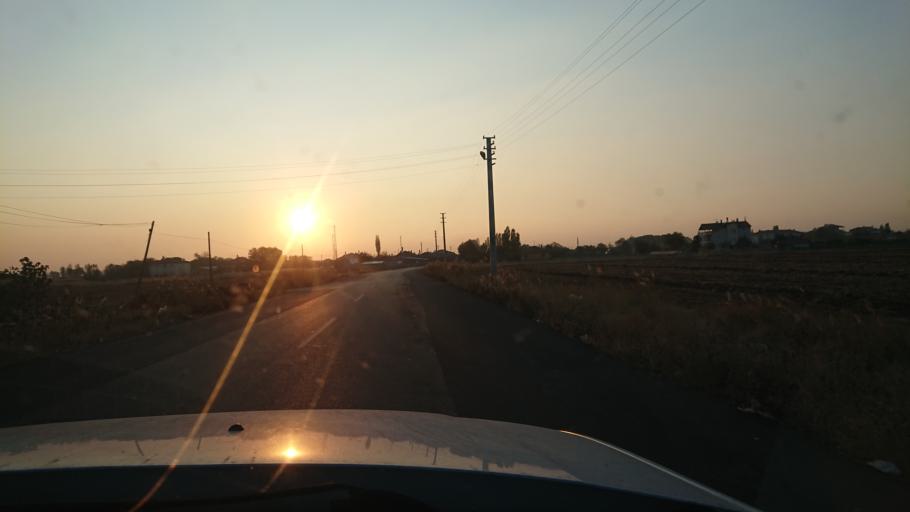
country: TR
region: Aksaray
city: Aksaray
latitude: 38.2998
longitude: 34.0772
